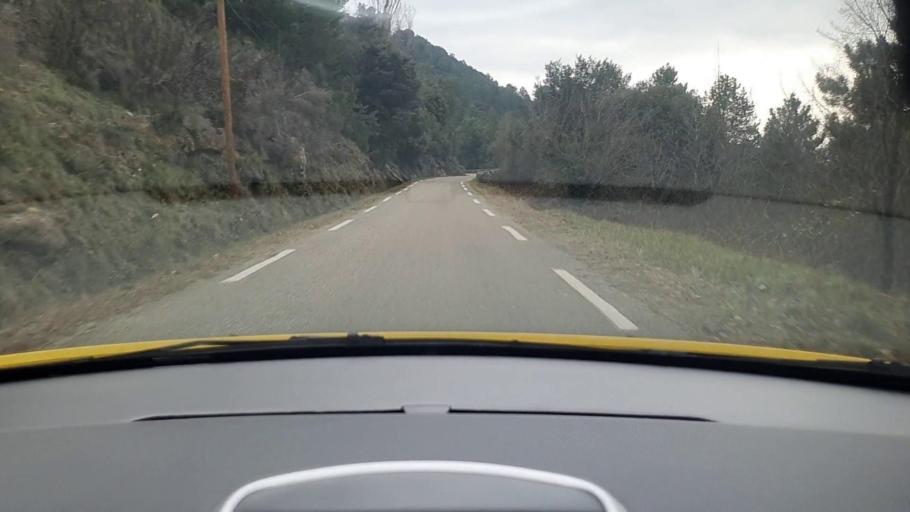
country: FR
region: Languedoc-Roussillon
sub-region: Departement du Gard
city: Besseges
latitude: 44.3487
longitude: 4.0219
